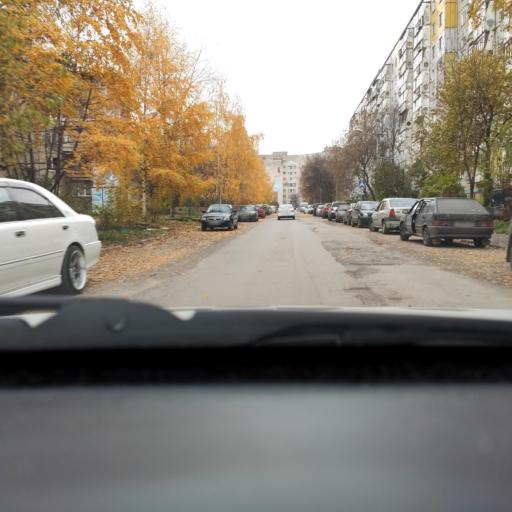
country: RU
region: Perm
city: Kondratovo
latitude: 57.9654
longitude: 56.1658
